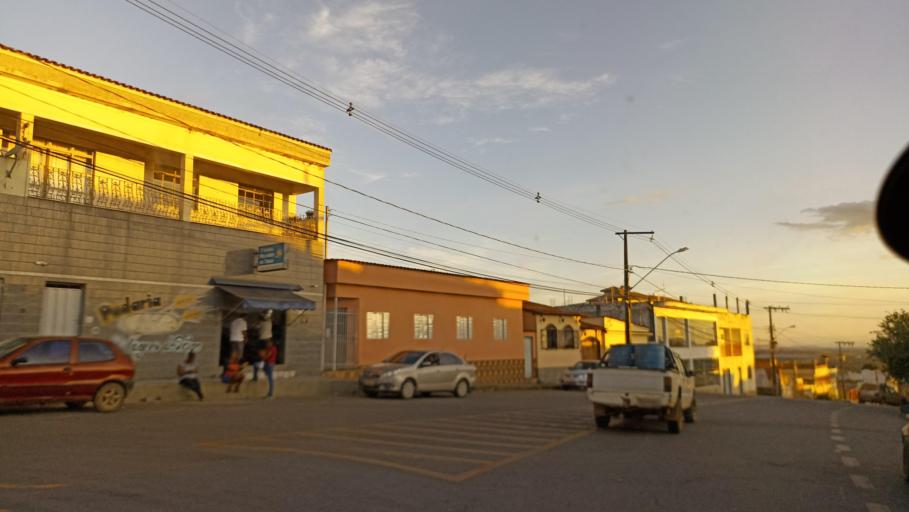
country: BR
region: Minas Gerais
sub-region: Sao Joao Del Rei
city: Sao Joao del Rei
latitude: -21.2441
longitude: -44.4158
